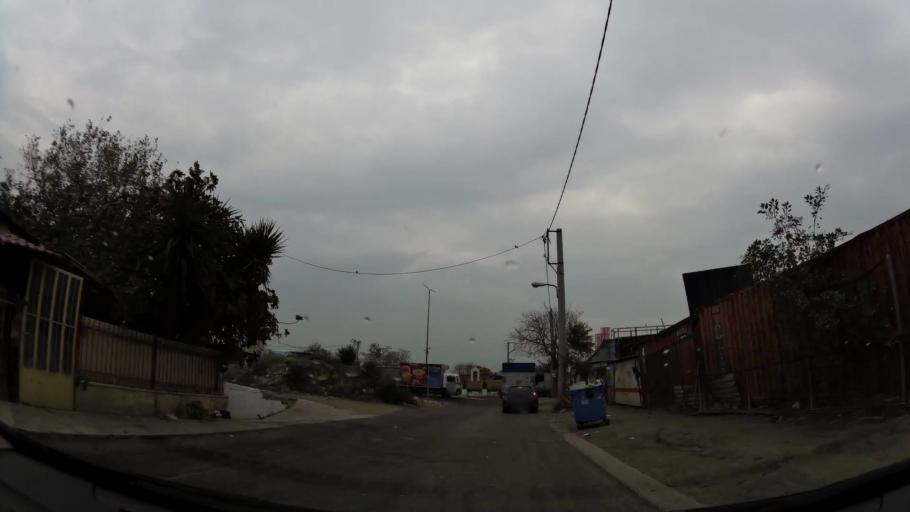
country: GR
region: Attica
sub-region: Nomarchia Athinas
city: Aigaleo
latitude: 37.9815
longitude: 23.6890
